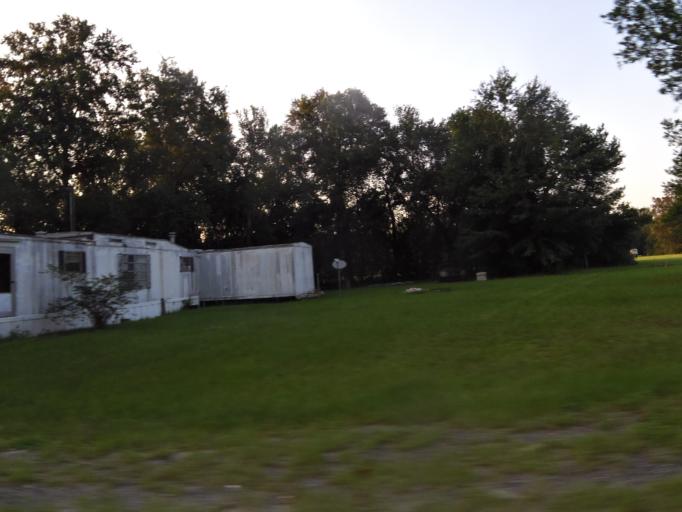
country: US
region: Florida
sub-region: Baker County
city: Macclenny
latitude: 30.3949
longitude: -82.1257
